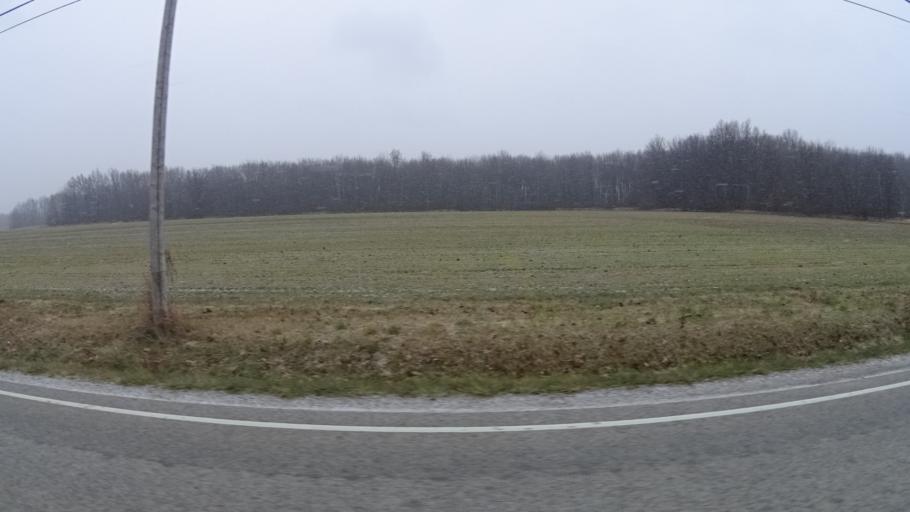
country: US
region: Ohio
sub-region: Lorain County
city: Oberlin
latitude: 41.3089
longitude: -82.2266
